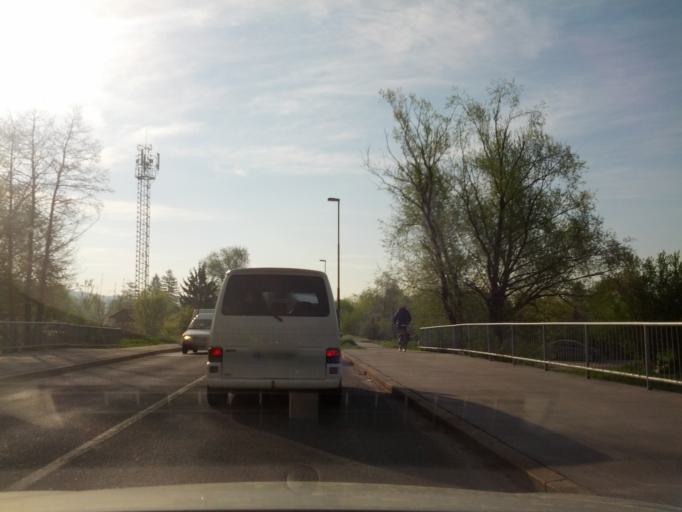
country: SI
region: Ljubljana
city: Ljubljana
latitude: 46.0365
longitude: 14.5061
